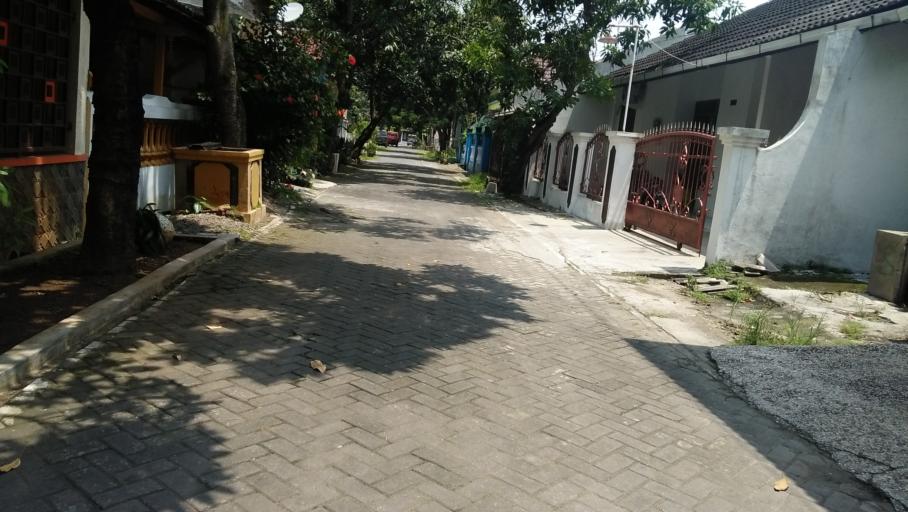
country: ID
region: Central Java
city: Mranggen
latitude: -7.0306
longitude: 110.4615
